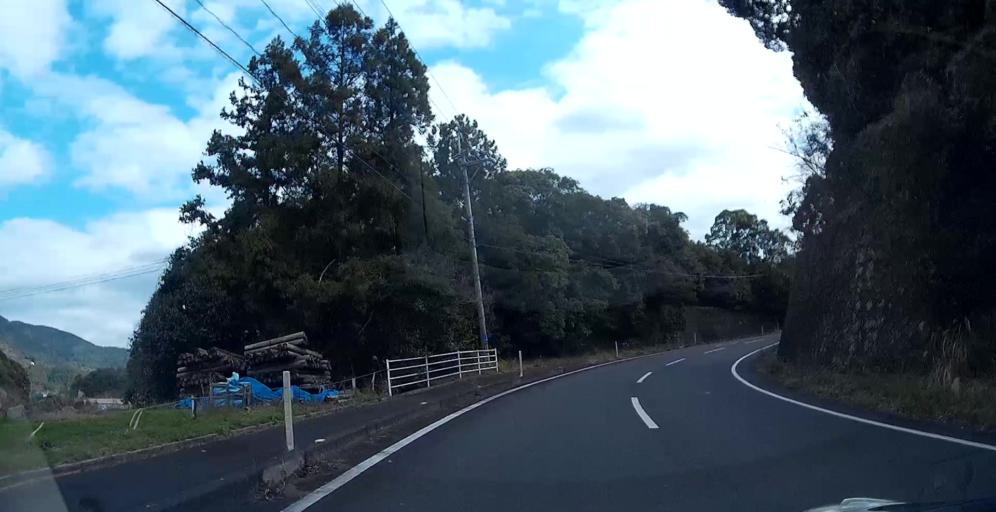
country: JP
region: Kumamoto
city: Minamata
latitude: 32.2303
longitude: 130.4300
